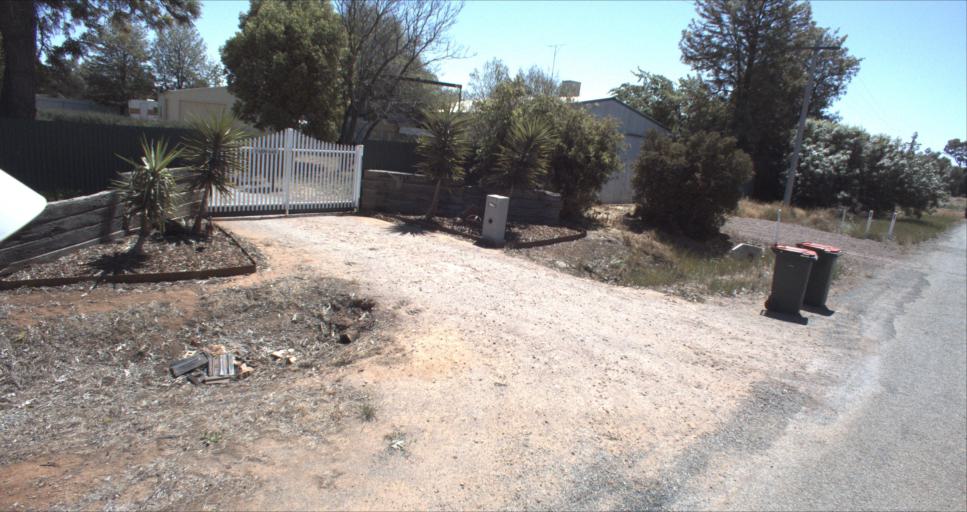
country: AU
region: New South Wales
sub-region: Leeton
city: Leeton
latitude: -34.5282
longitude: 146.3320
